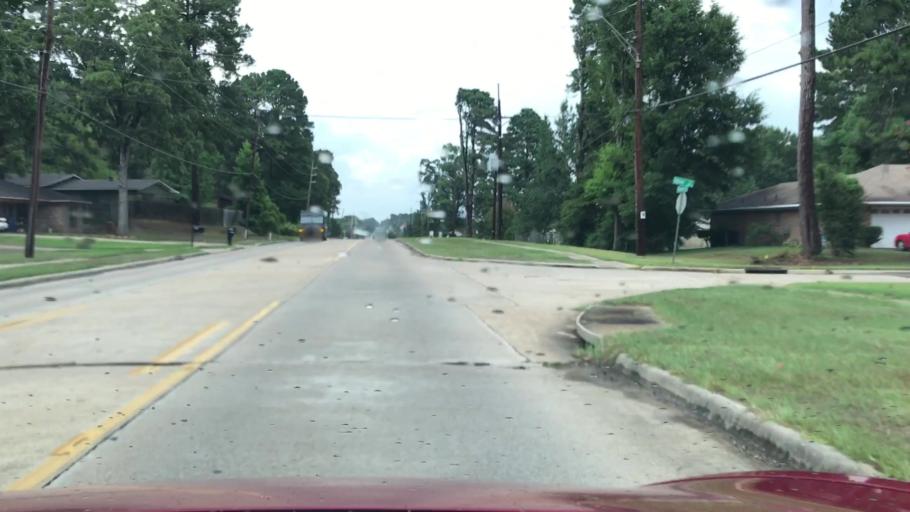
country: US
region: Louisiana
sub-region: De Soto Parish
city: Stonewall
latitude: 32.3972
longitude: -93.7804
